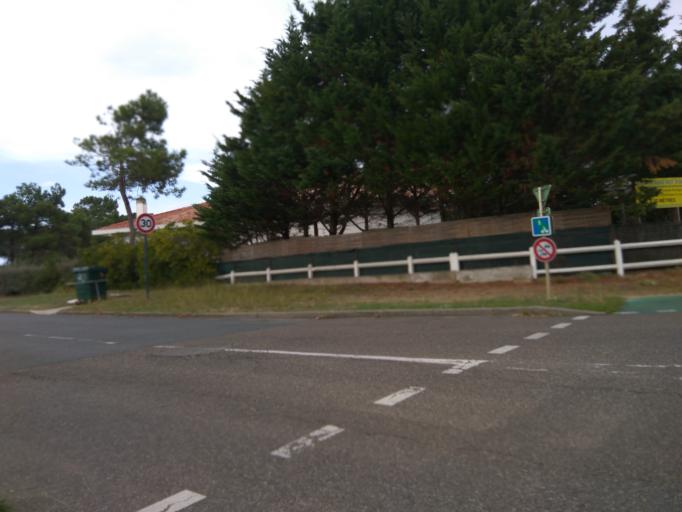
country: FR
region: Aquitaine
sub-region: Departement des Landes
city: Capbreton
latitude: 43.6413
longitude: -1.4418
